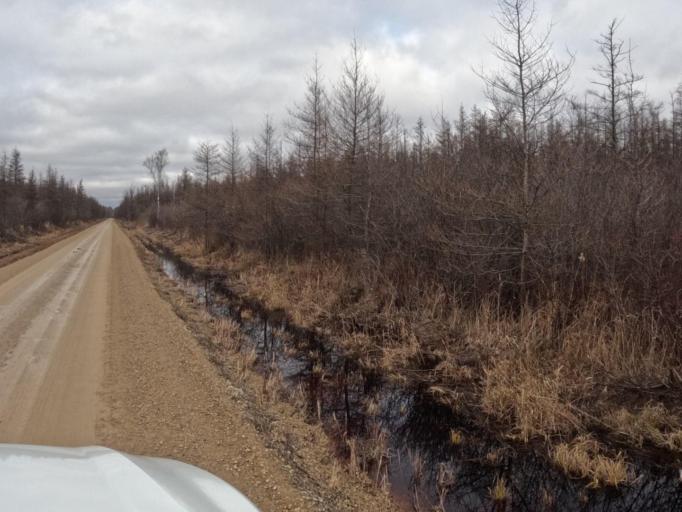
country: CA
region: Ontario
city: Shelburne
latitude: 43.8978
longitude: -80.4081
